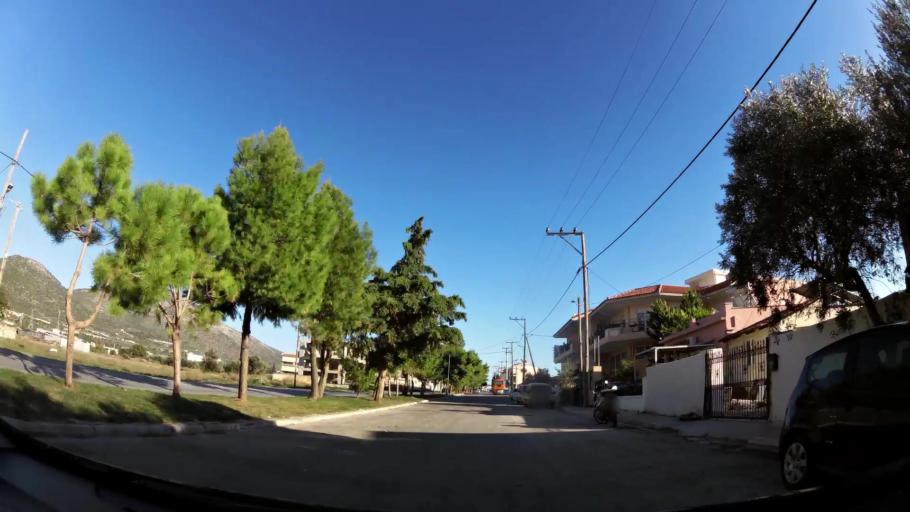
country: GR
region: Attica
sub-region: Nomarchia Anatolikis Attikis
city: Kalyvia Thorikou
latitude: 37.8449
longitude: 23.9257
